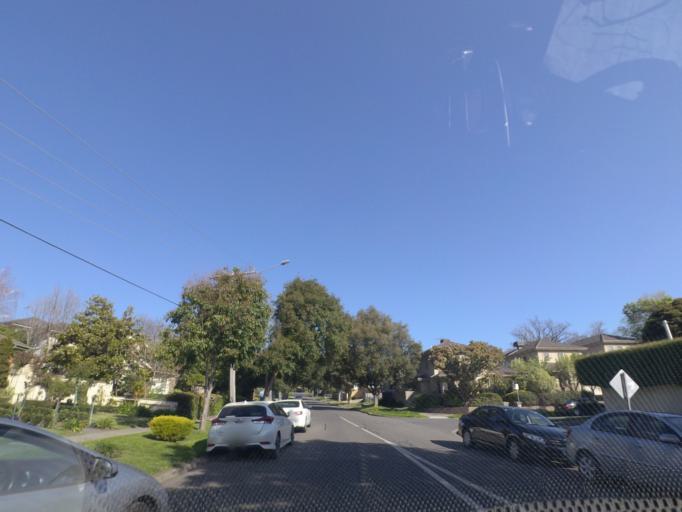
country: AU
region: Victoria
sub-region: Whitehorse
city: Mont Albert North
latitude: -37.7984
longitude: 145.1035
